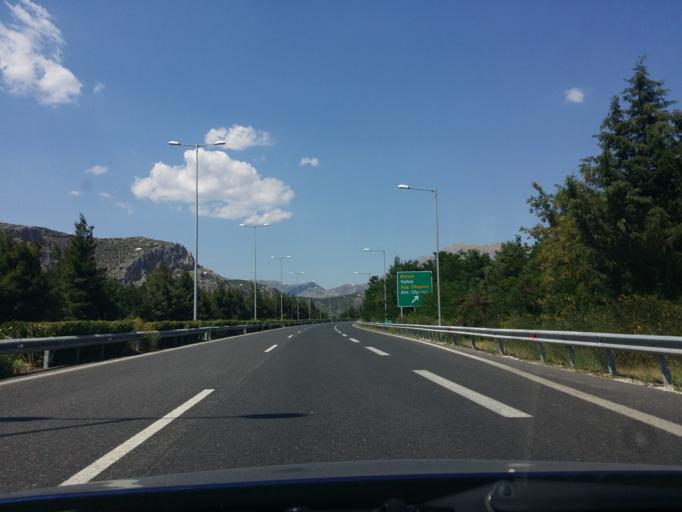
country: GR
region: Peloponnese
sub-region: Nomos Arkadias
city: Tripoli
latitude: 37.5869
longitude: 22.4344
